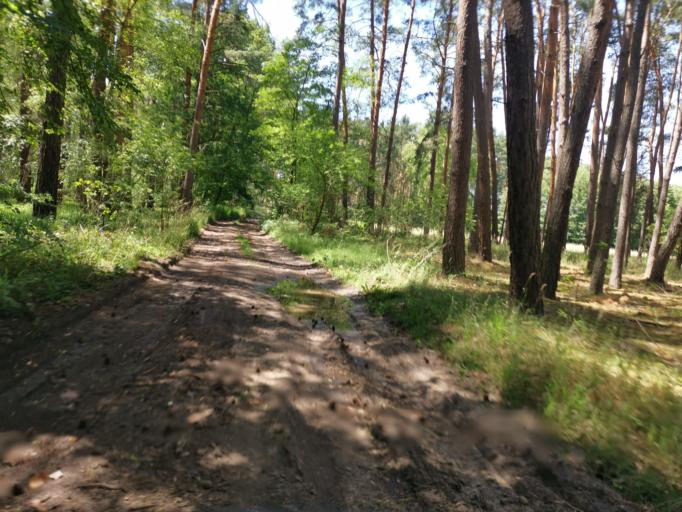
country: CZ
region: South Moravian
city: Vracov
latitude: 48.9665
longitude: 17.2331
